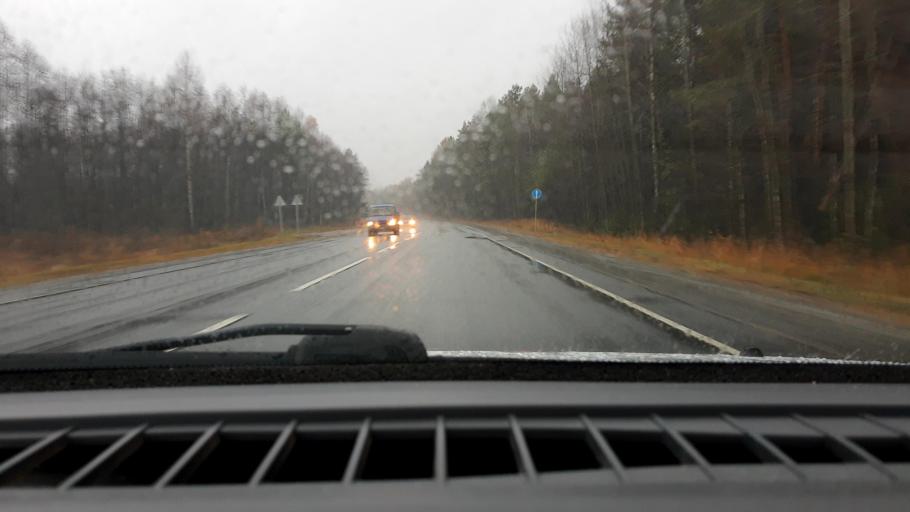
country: RU
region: Nizjnij Novgorod
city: Linda
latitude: 56.6668
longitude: 44.1356
